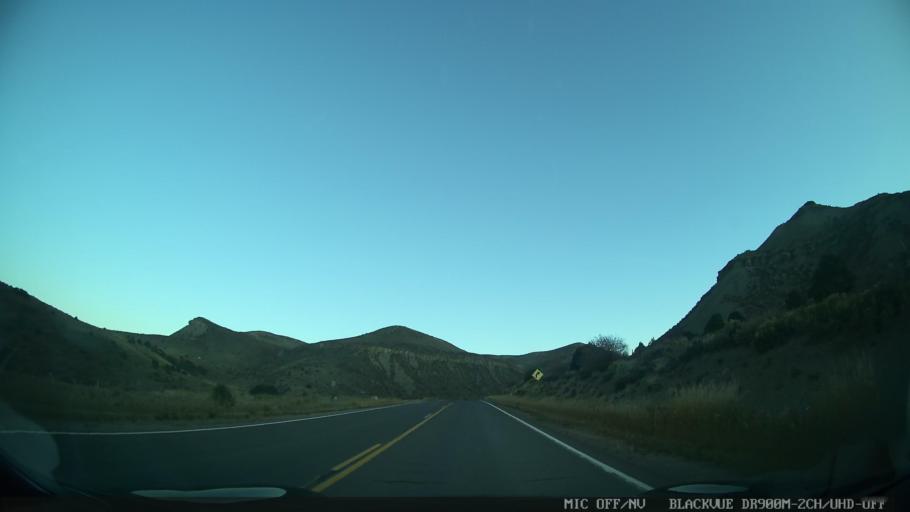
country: US
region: Colorado
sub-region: Eagle County
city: Edwards
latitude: 39.7702
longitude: -106.6815
